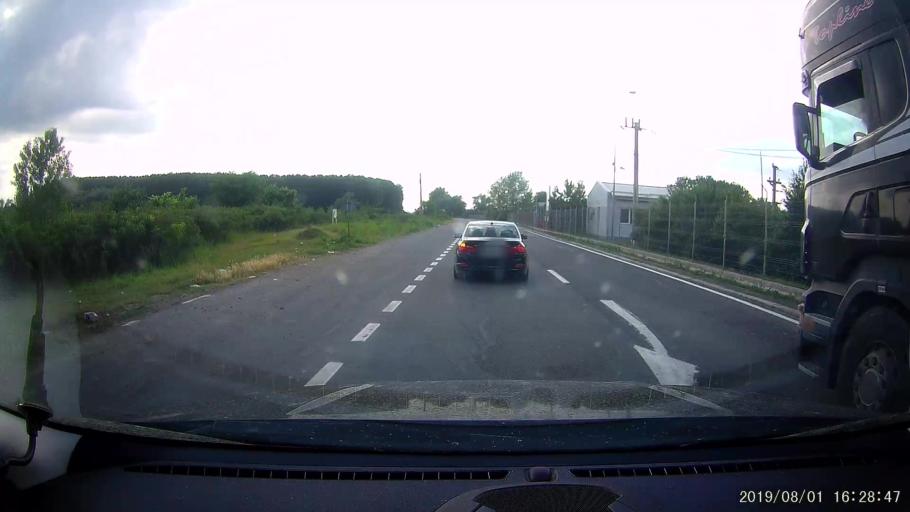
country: BG
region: Silistra
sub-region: Obshtina Silistra
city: Silistra
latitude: 44.1460
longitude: 27.3025
